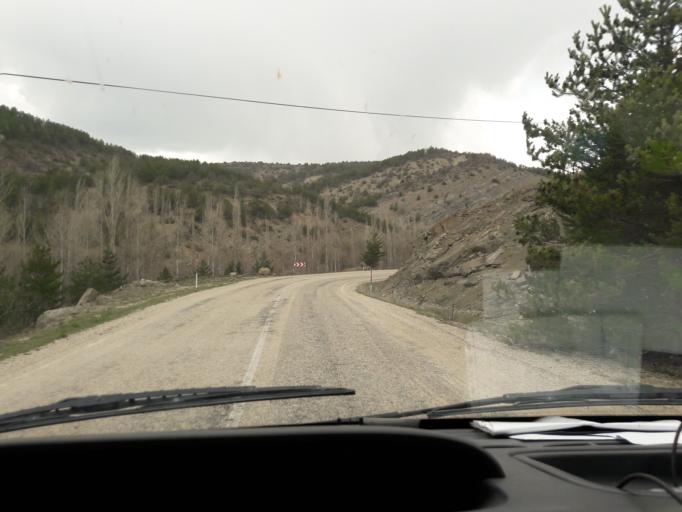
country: TR
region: Giresun
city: Alucra
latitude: 40.2816
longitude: 38.8199
